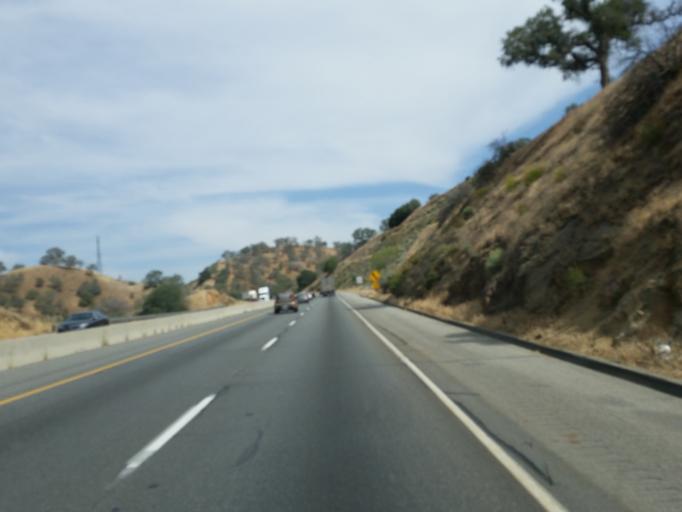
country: US
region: California
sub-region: Kern County
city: Bear Valley Springs
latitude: 35.2582
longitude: -118.6148
